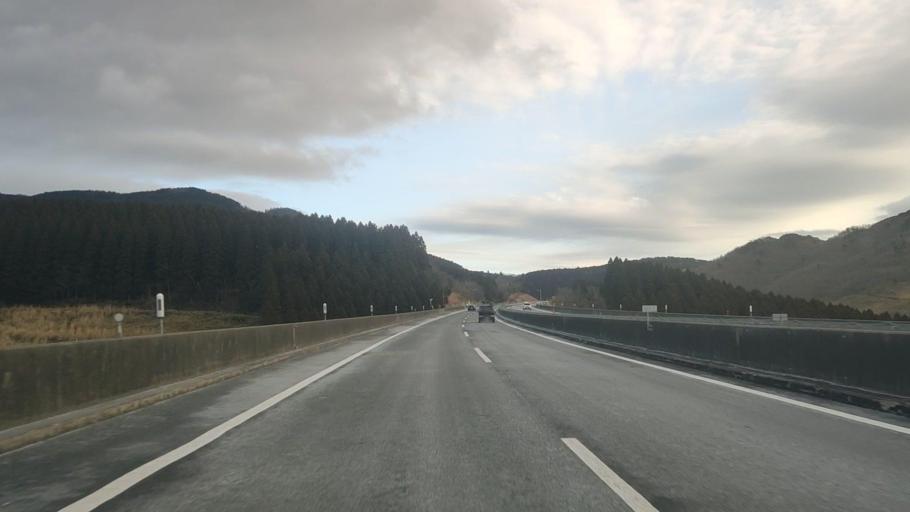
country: JP
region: Oita
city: Beppu
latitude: 33.2860
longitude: 131.3473
